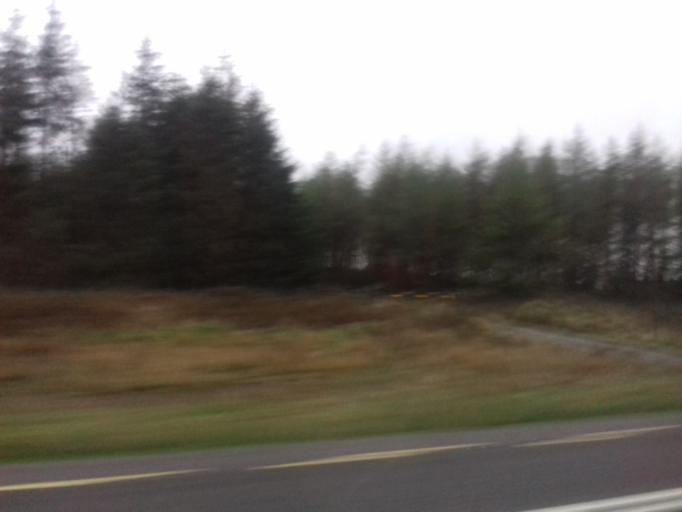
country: IE
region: Munster
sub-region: Ciarrai
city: Castleisland
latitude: 52.2805
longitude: -9.4078
